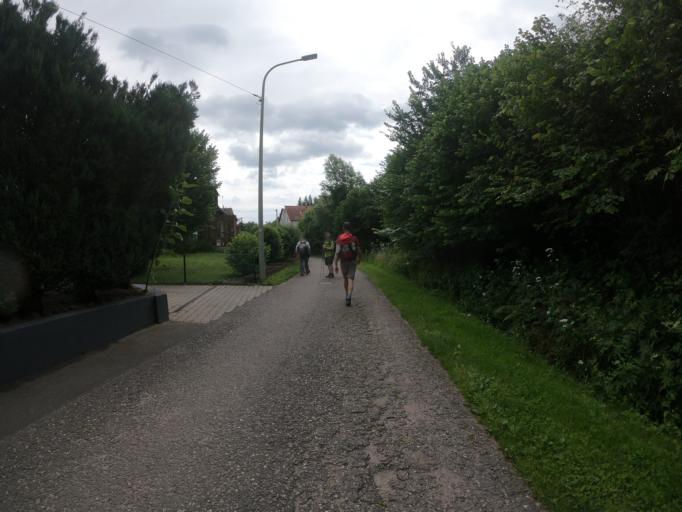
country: DE
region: Rheinland-Pfalz
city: Bad Bergzabern
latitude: 49.1134
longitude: 7.9964
